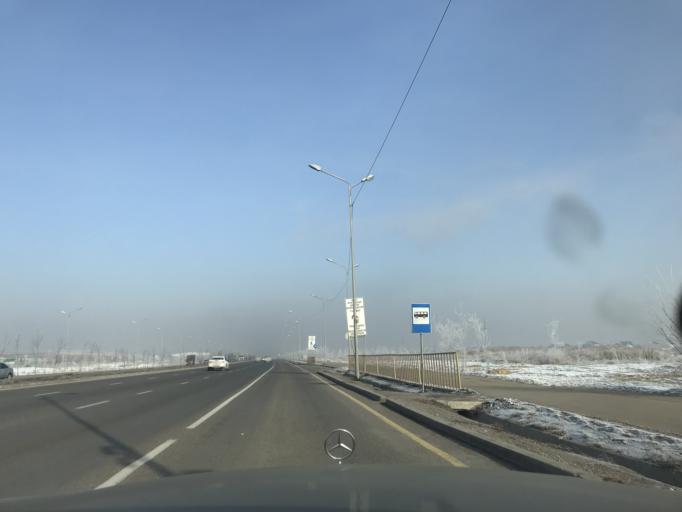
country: KZ
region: Almaty Oblysy
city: Burunday
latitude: 43.3213
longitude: 76.8340
